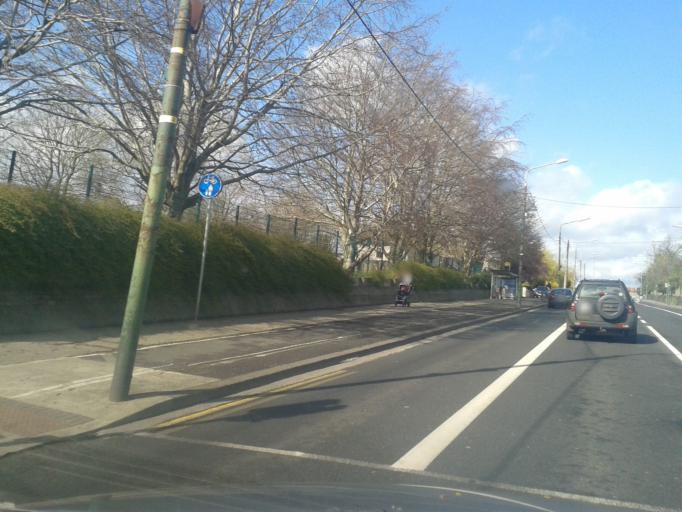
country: IE
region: Leinster
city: Drumcondra
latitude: 53.3790
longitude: -6.2470
